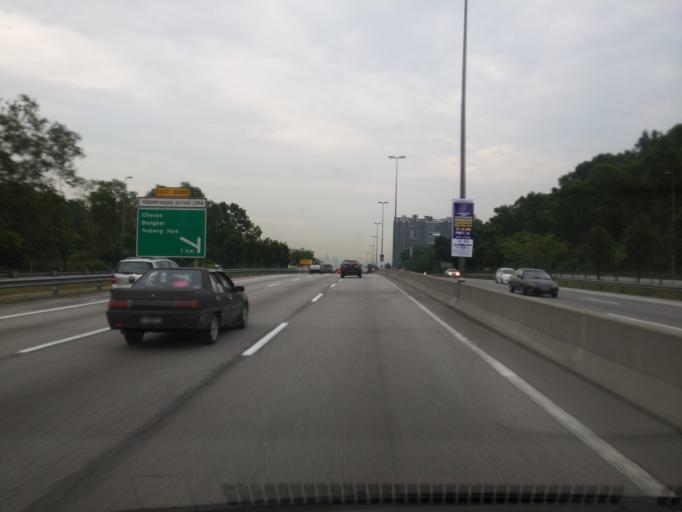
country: MY
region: Kuala Lumpur
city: Kuala Lumpur
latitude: 3.0789
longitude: 101.6912
